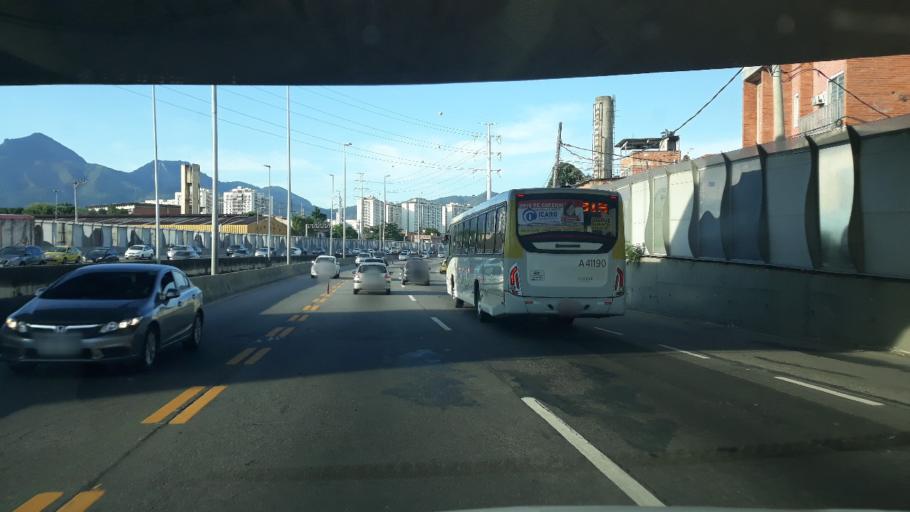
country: BR
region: Rio de Janeiro
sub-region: Rio De Janeiro
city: Rio de Janeiro
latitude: -22.8779
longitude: -43.2772
